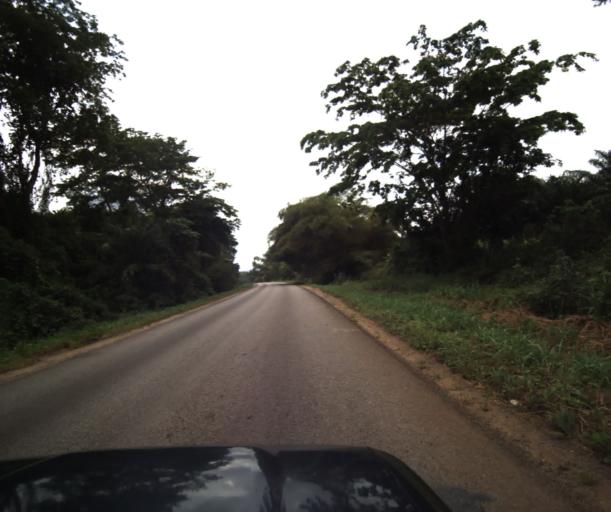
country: CM
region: Centre
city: Eseka
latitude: 3.8502
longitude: 10.4903
